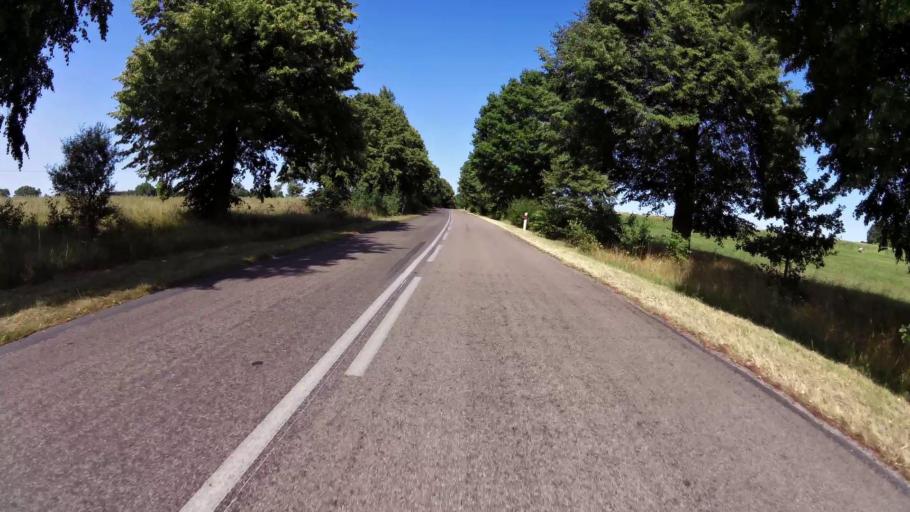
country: PL
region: West Pomeranian Voivodeship
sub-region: Powiat stargardzki
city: Dobrzany
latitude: 53.3260
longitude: 15.3894
